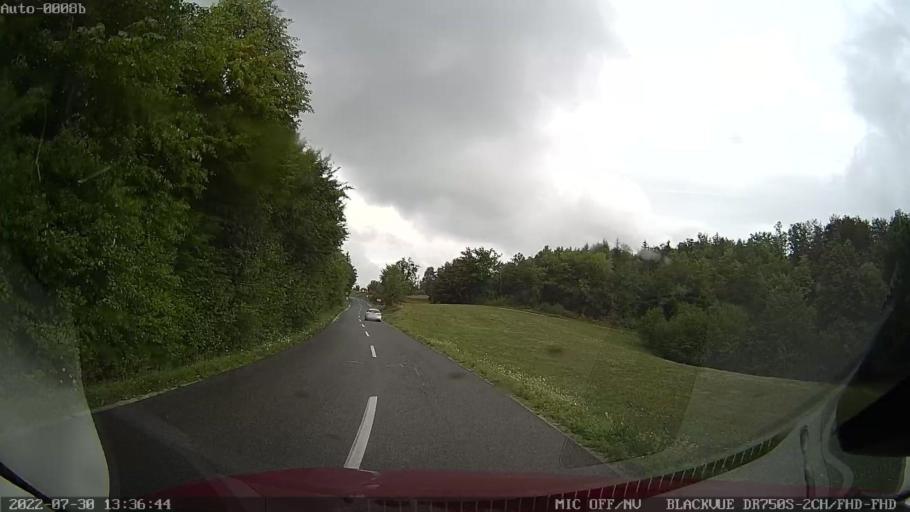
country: SI
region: Zuzemberk
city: Zuzemberk
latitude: 45.8721
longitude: 14.9224
